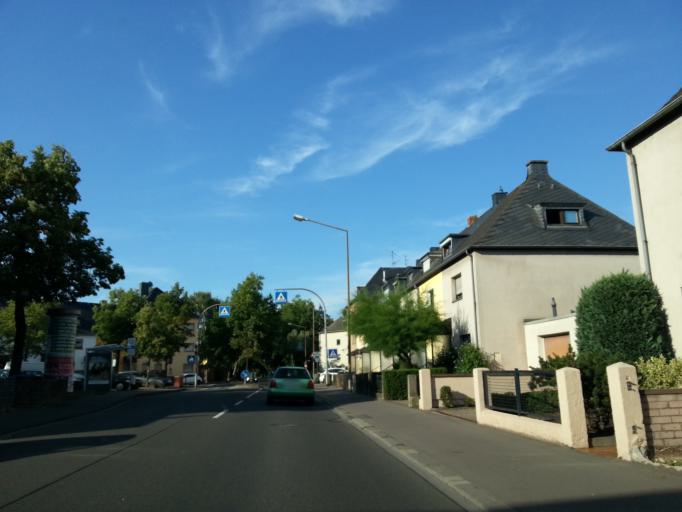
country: DE
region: Rheinland-Pfalz
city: Trier
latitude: 49.7670
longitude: 6.6637
